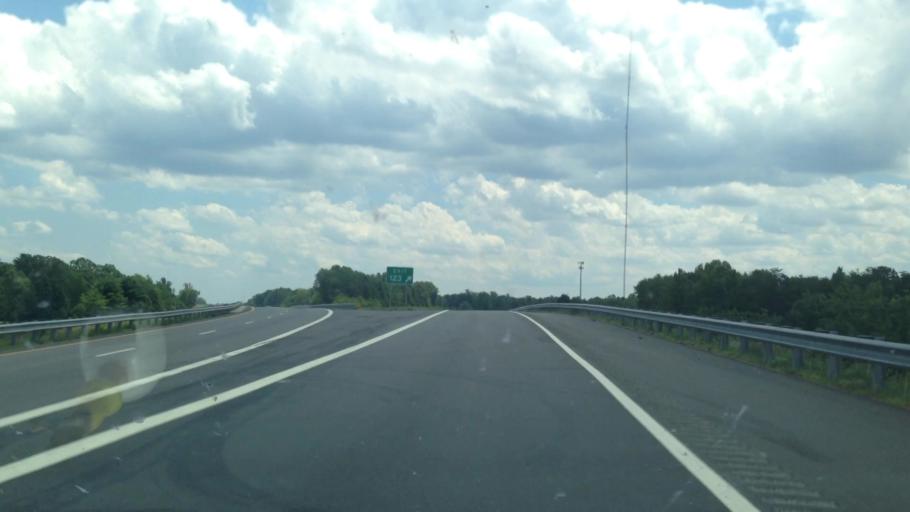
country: US
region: North Carolina
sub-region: Guilford County
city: Stokesdale
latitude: 36.2861
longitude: -79.9407
